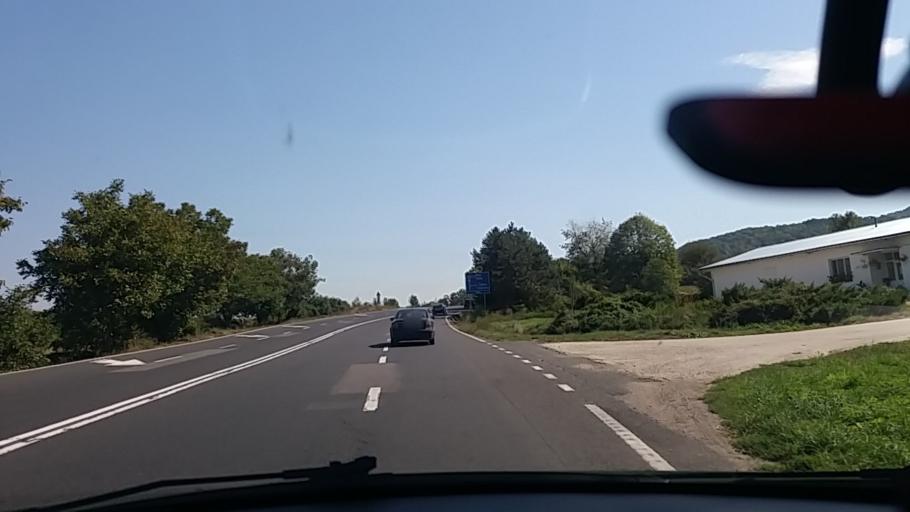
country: RO
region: Hunedoara
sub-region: Comuna Soimus
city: Soimus
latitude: 45.9099
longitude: 22.8648
